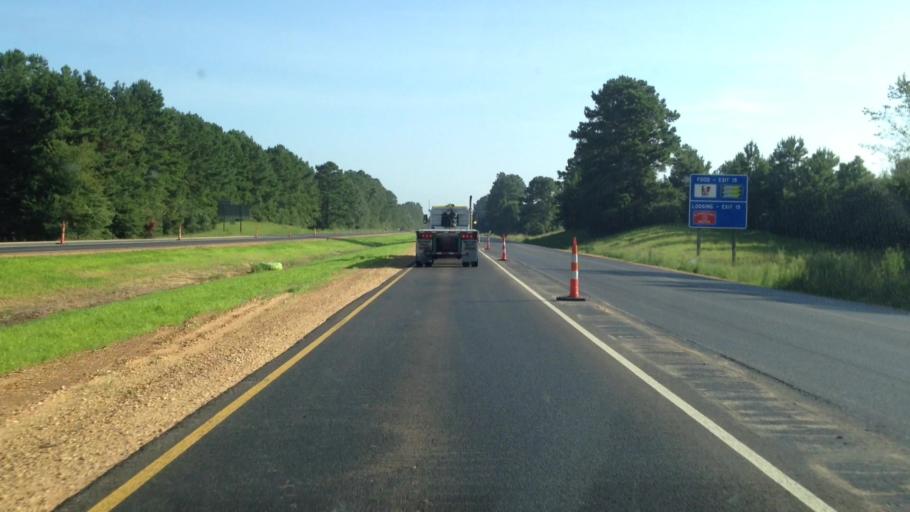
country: US
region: Mississippi
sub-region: Pike County
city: McComb
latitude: 31.2060
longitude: -90.4839
